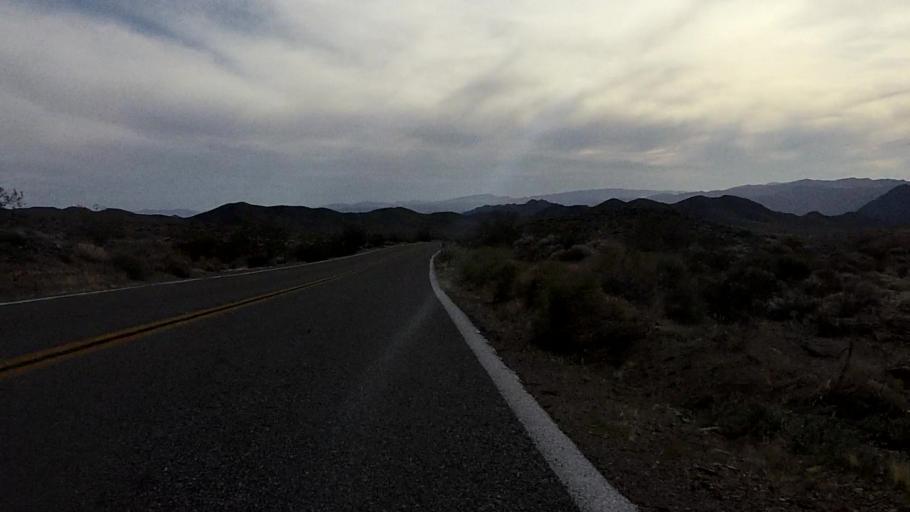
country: US
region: Nevada
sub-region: Nye County
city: Pahrump
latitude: 35.9171
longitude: -116.4384
